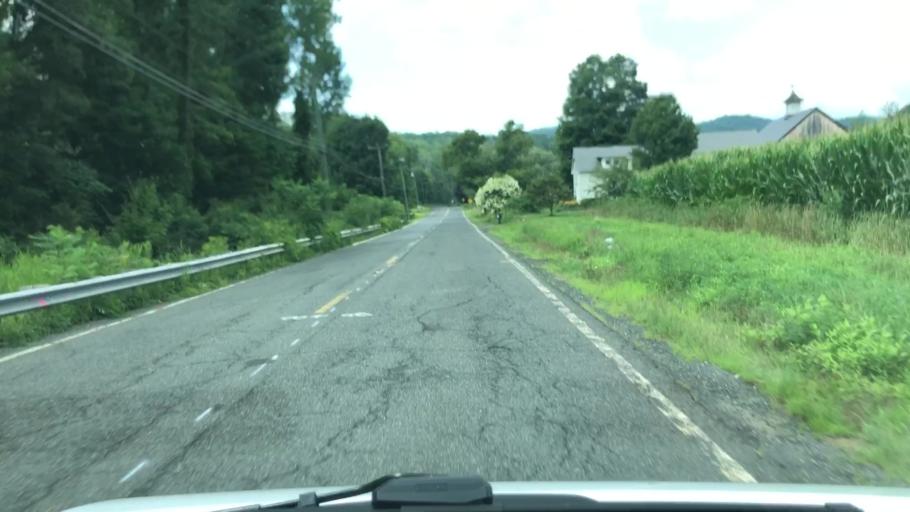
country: US
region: Massachusetts
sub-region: Franklin County
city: Conway
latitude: 42.5120
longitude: -72.7152
